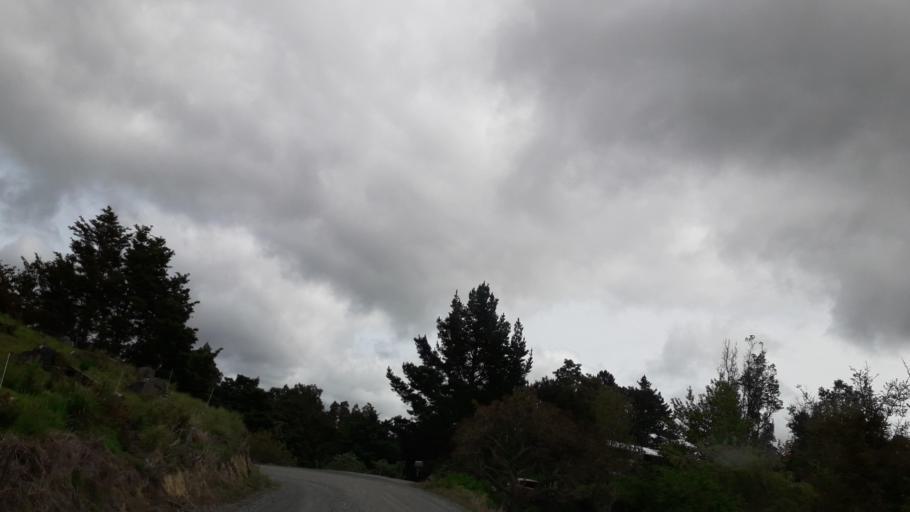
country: NZ
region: Northland
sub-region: Far North District
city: Kerikeri
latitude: -35.1309
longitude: 173.7183
